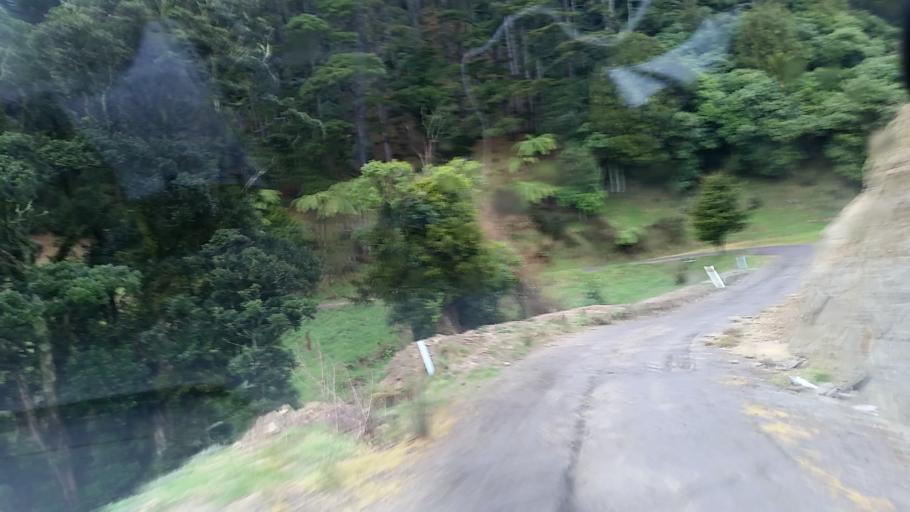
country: NZ
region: Taranaki
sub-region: South Taranaki District
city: Eltham
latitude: -39.4728
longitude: 174.4174
